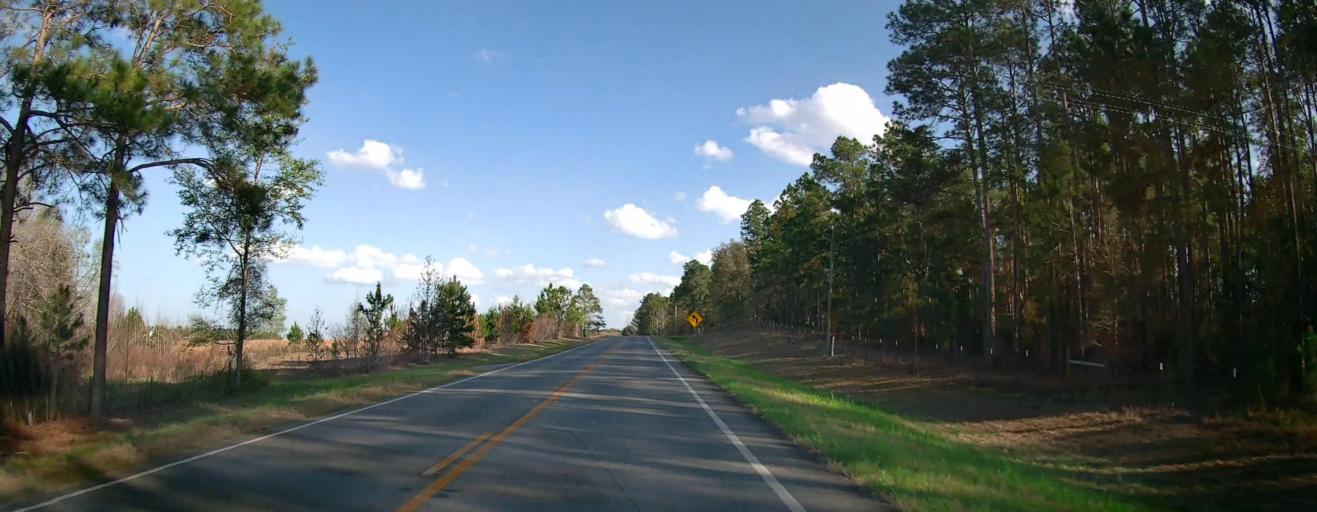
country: US
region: Georgia
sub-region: Toombs County
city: Lyons
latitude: 32.1777
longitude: -82.2874
